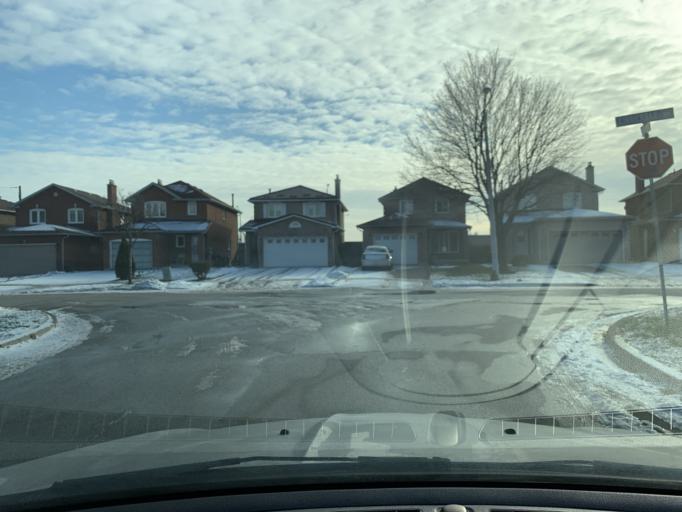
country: CA
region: Ontario
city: Etobicoke
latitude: 43.7199
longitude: -79.6186
